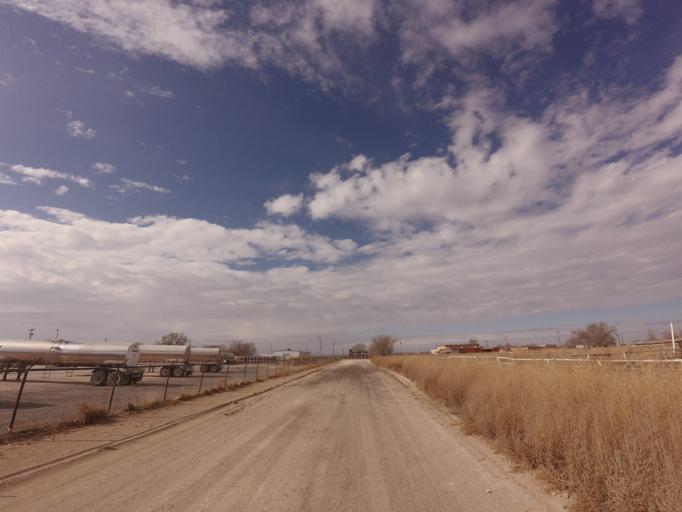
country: US
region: New Mexico
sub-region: Curry County
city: Clovis
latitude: 34.3928
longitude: -103.2184
